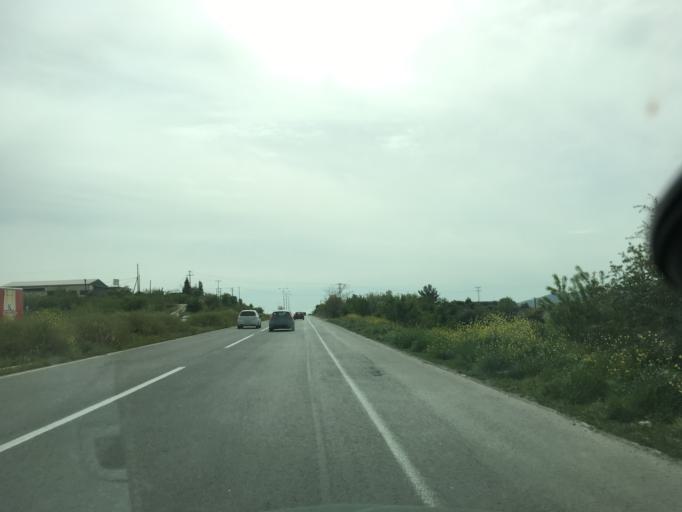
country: GR
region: Thessaly
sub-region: Nomos Magnisias
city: Nea Ionia
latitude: 39.3835
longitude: 22.8505
